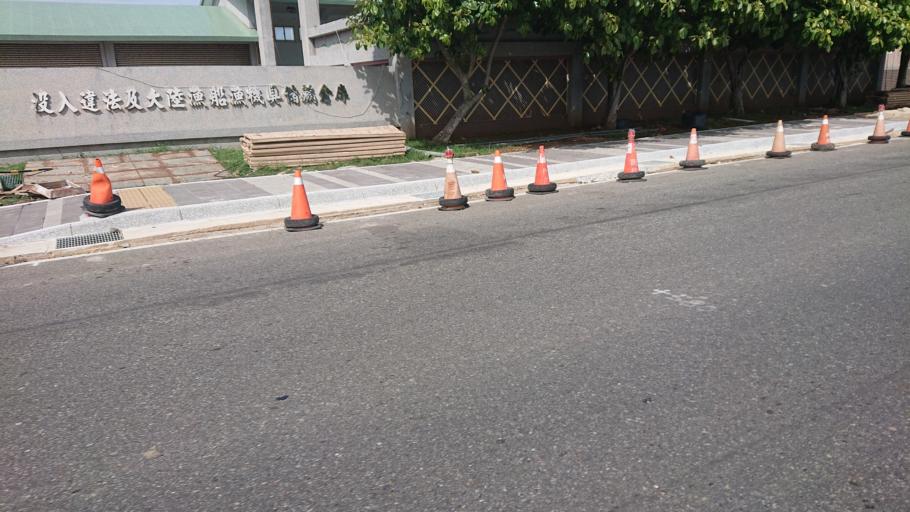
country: TW
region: Taiwan
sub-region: Penghu
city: Ma-kung
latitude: 23.5650
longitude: 119.5782
